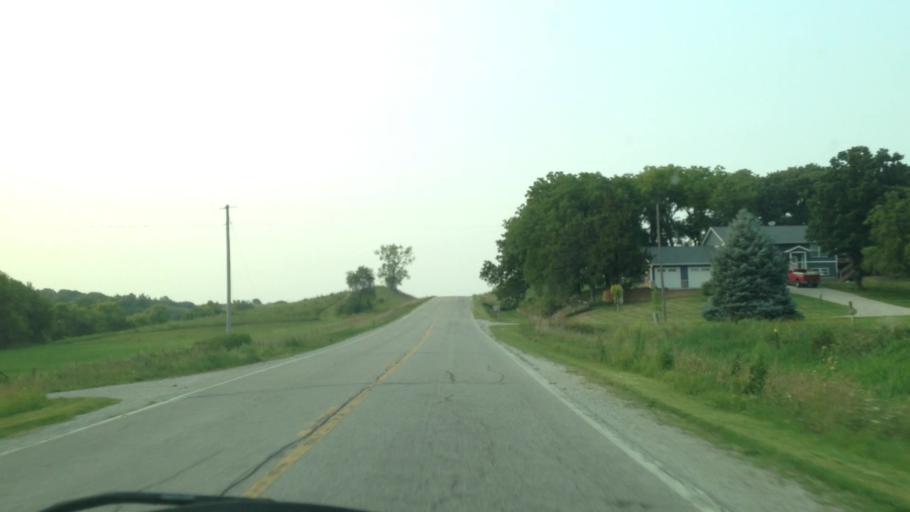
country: US
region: Iowa
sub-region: Iowa County
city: Marengo
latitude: 41.8769
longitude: -92.0890
